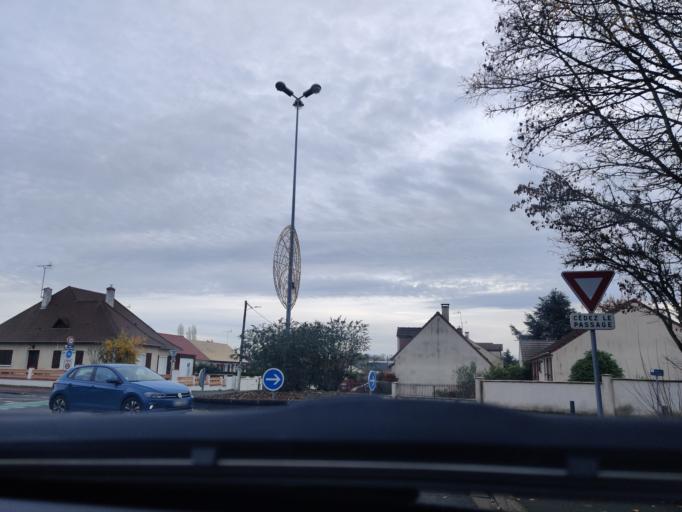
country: FR
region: Centre
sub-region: Departement du Loiret
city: La Chapelle-Saint-Mesmin
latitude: 47.8894
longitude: 1.8296
